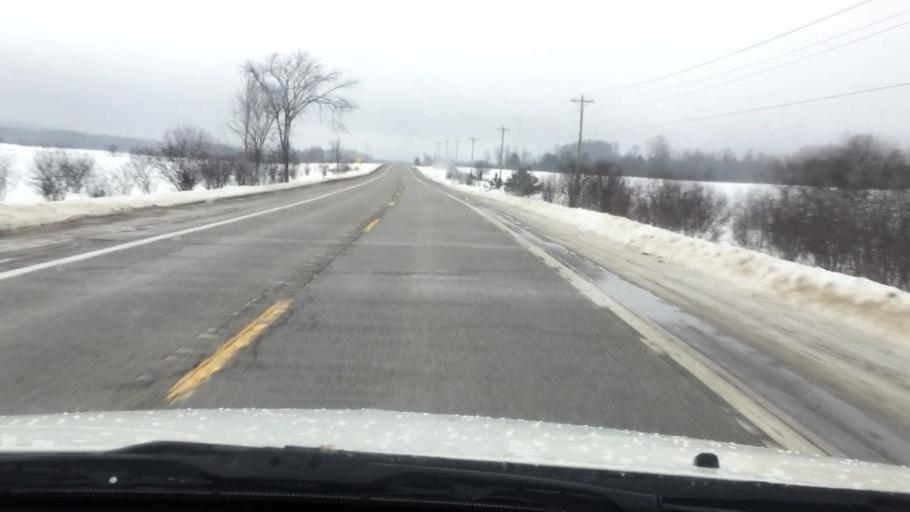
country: US
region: Michigan
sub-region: Charlevoix County
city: East Jordan
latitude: 45.1287
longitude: -85.1373
